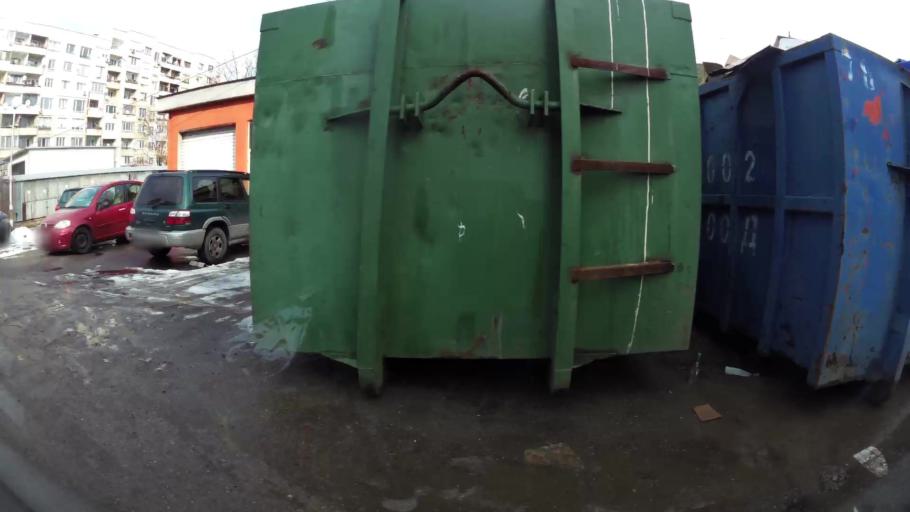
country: BG
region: Sofia-Capital
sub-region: Stolichna Obshtina
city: Sofia
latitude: 42.7164
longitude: 23.2718
